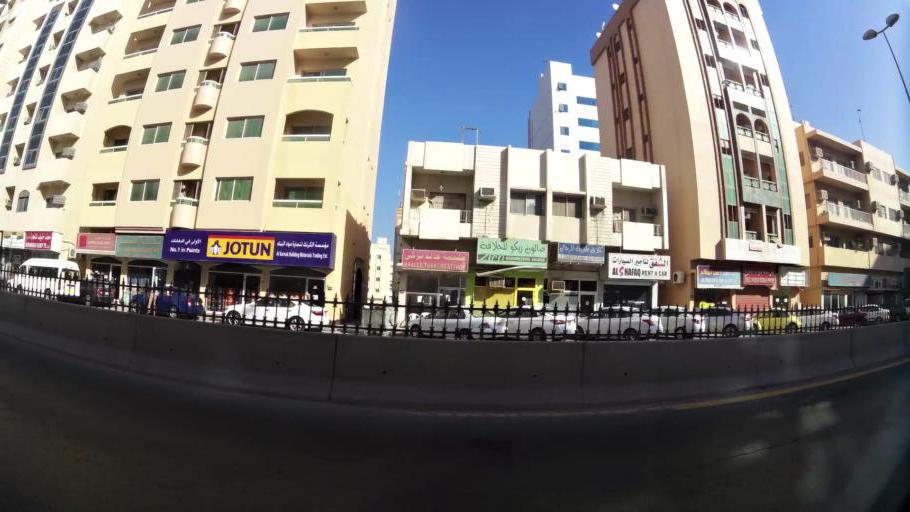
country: AE
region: Ash Shariqah
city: Sharjah
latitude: 25.3699
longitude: 55.3970
